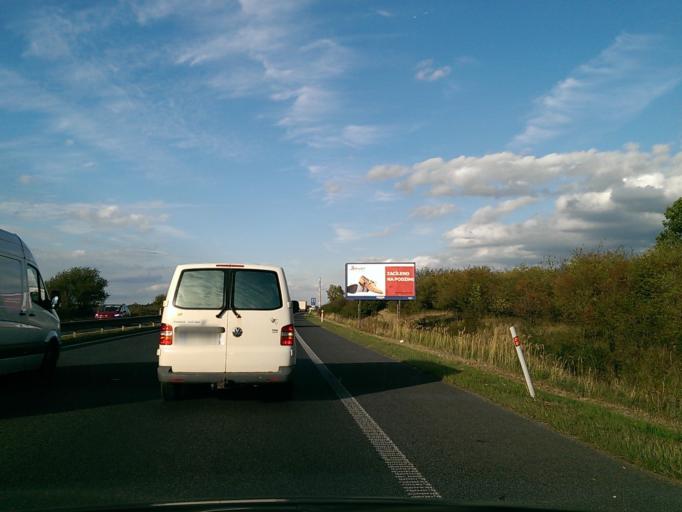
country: CZ
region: Central Bohemia
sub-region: Okres Mlada Boleslav
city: Mlada Boleslav
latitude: 50.3916
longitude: 14.9070
